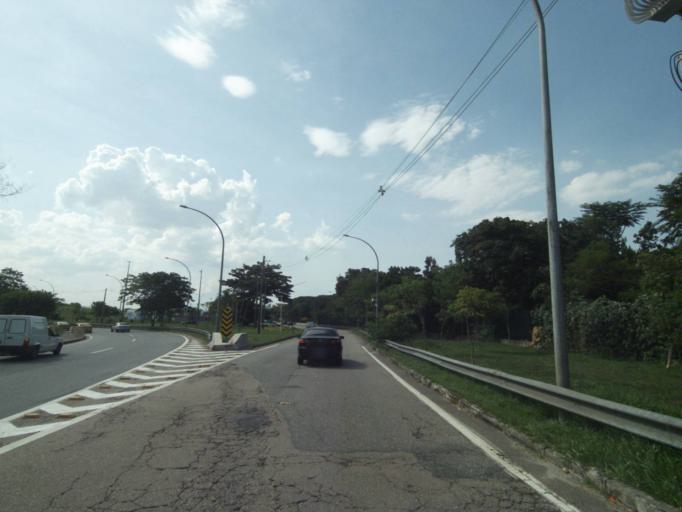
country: BR
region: Rio de Janeiro
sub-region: Rio De Janeiro
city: Rio de Janeiro
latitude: -22.8601
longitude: -43.2325
